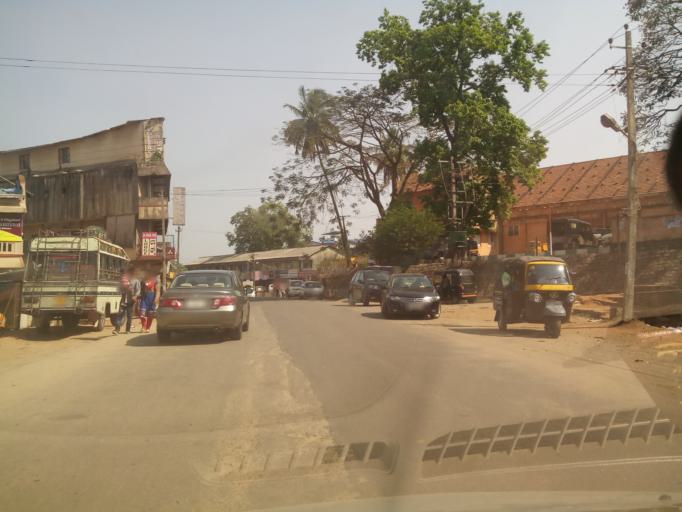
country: IN
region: Karnataka
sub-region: Hassan
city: Sakleshpur
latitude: 12.9470
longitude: 75.7869
